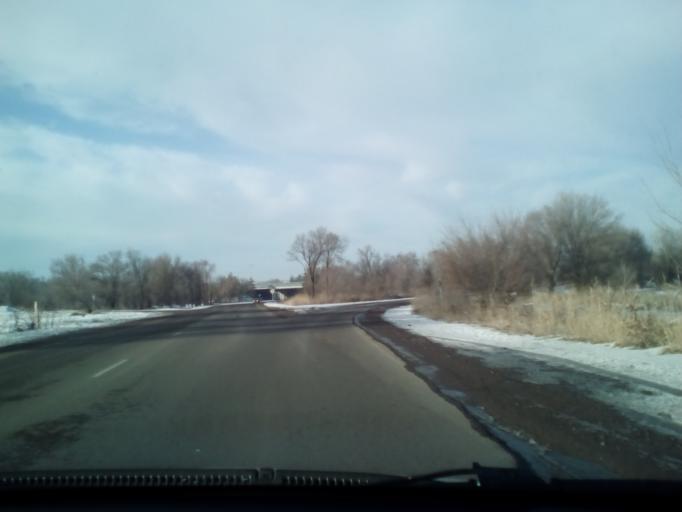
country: KZ
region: Almaty Oblysy
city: Burunday
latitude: 43.2200
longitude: 76.4102
